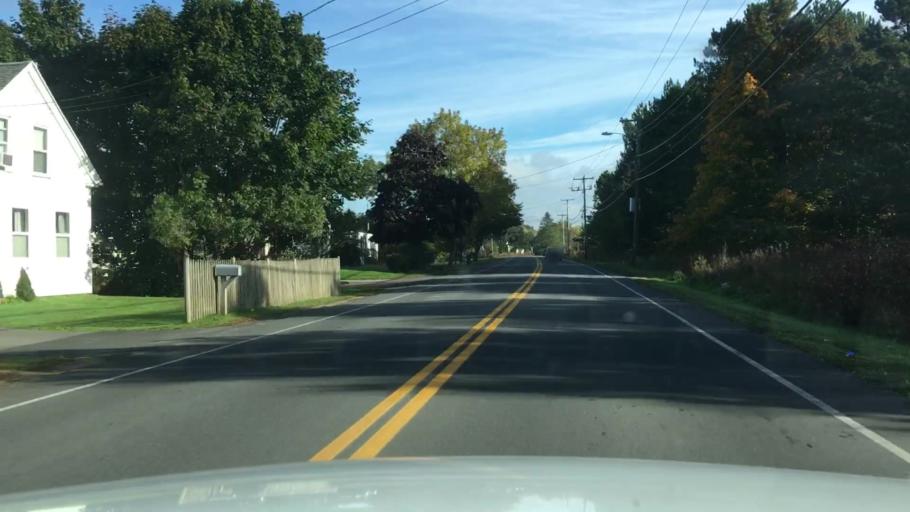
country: US
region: Maine
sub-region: Knox County
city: Thomaston
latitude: 44.0852
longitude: -69.1676
